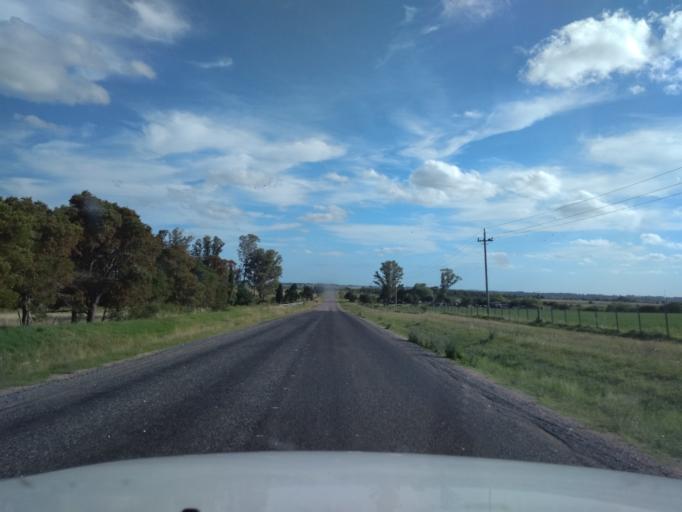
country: UY
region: Canelones
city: San Ramon
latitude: -34.2517
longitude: -55.9262
